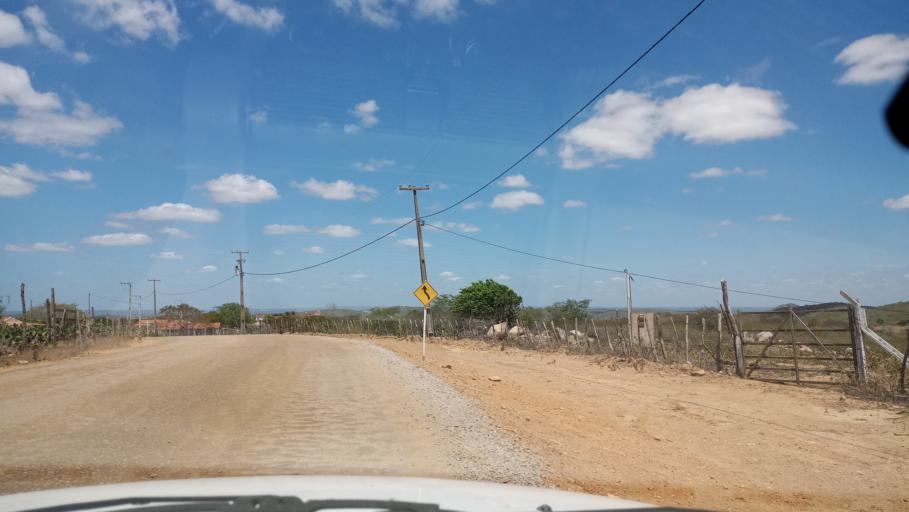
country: BR
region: Rio Grande do Norte
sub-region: Sao Paulo Do Potengi
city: Sao Paulo do Potengi
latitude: -5.7812
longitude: -35.9141
